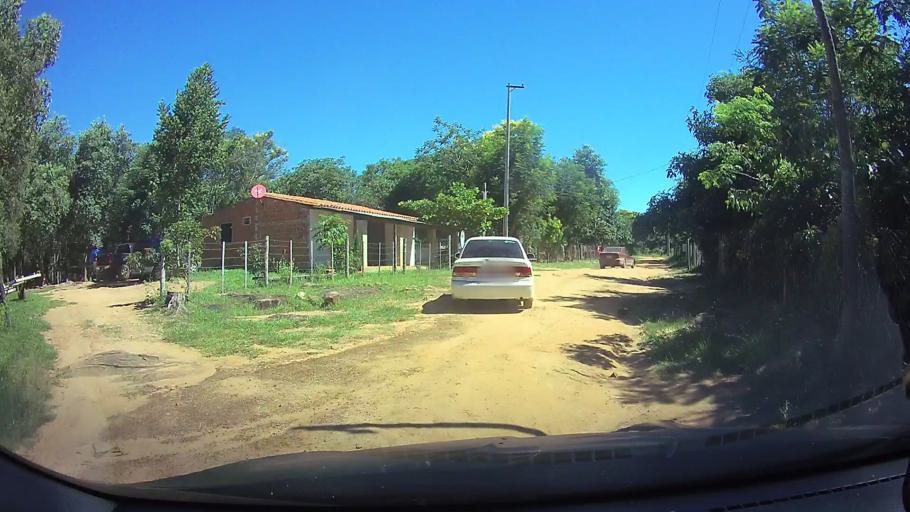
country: PY
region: Cordillera
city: Arroyos y Esteros
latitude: -24.9791
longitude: -57.2157
